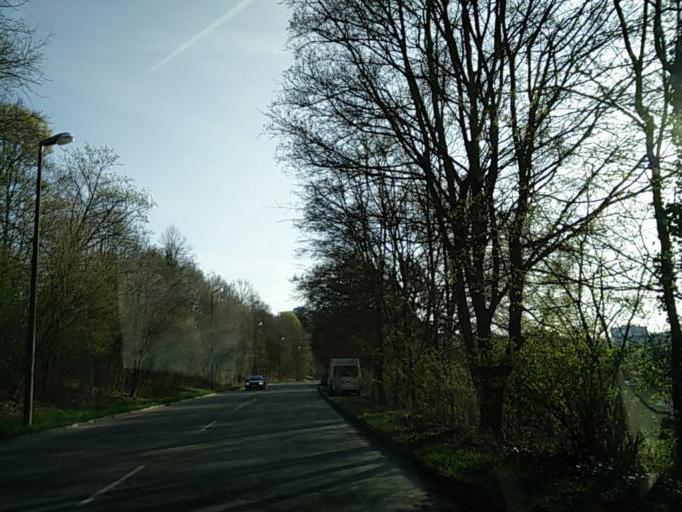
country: DE
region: Baden-Wuerttemberg
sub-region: Tuebingen Region
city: Tuebingen
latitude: 48.5420
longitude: 9.0411
